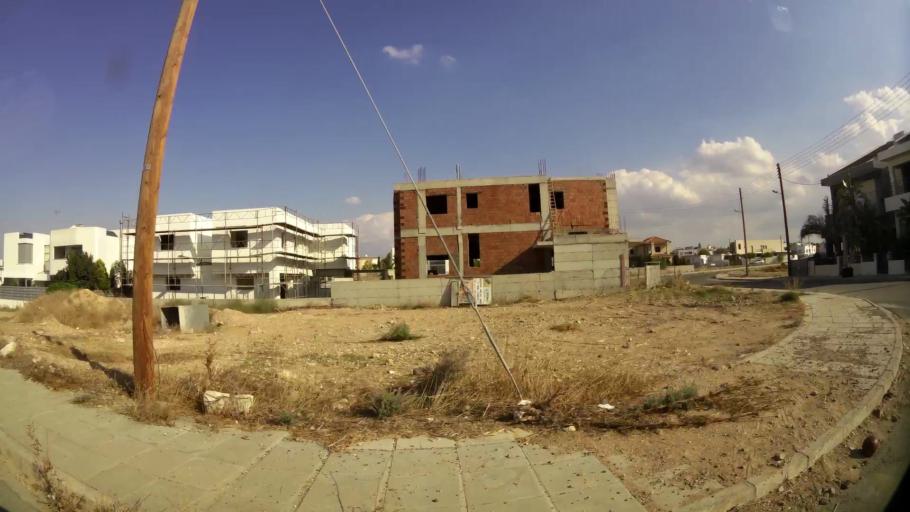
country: CY
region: Lefkosia
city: Kato Deftera
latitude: 35.1369
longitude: 33.2985
